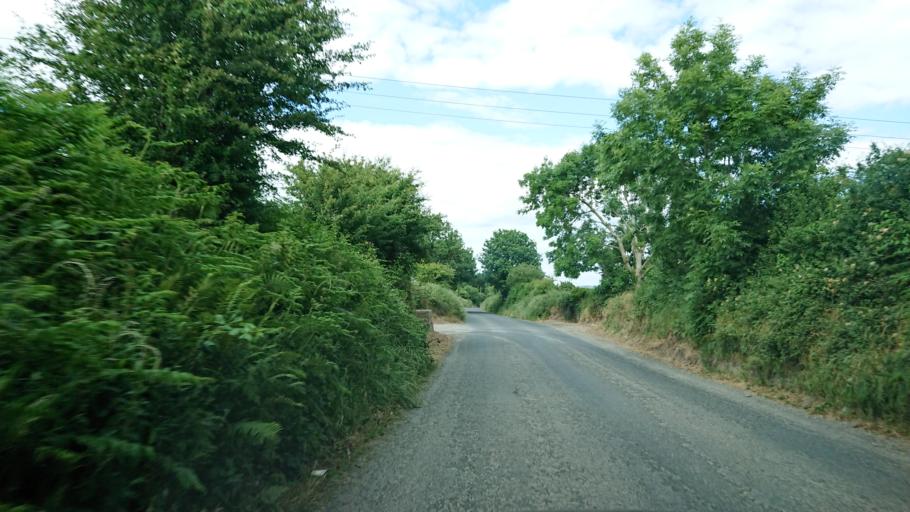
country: IE
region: Munster
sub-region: Waterford
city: Waterford
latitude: 52.2227
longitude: -7.1534
